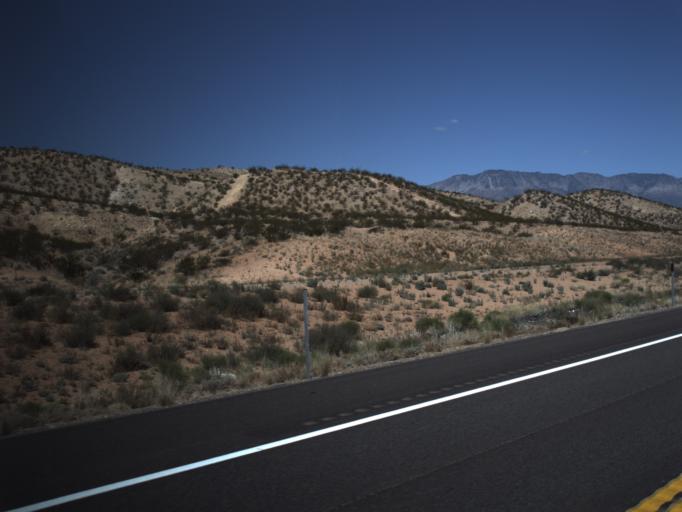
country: US
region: Utah
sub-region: Washington County
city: Washington
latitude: 37.1009
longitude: -113.4664
